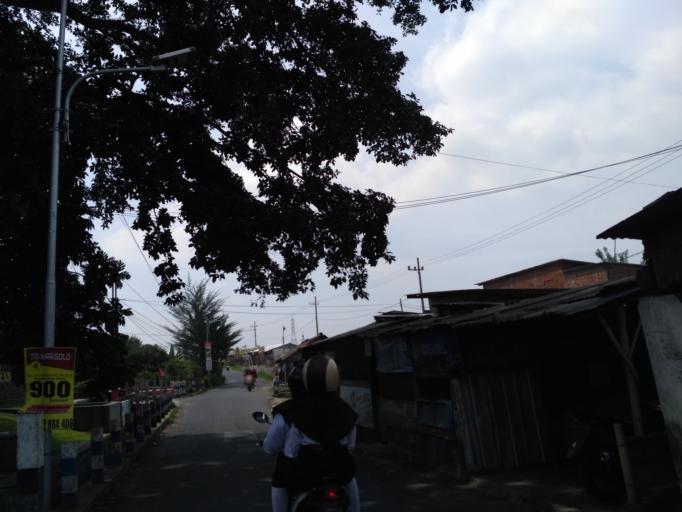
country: ID
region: East Java
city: Malang
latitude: -7.9354
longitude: 112.6282
